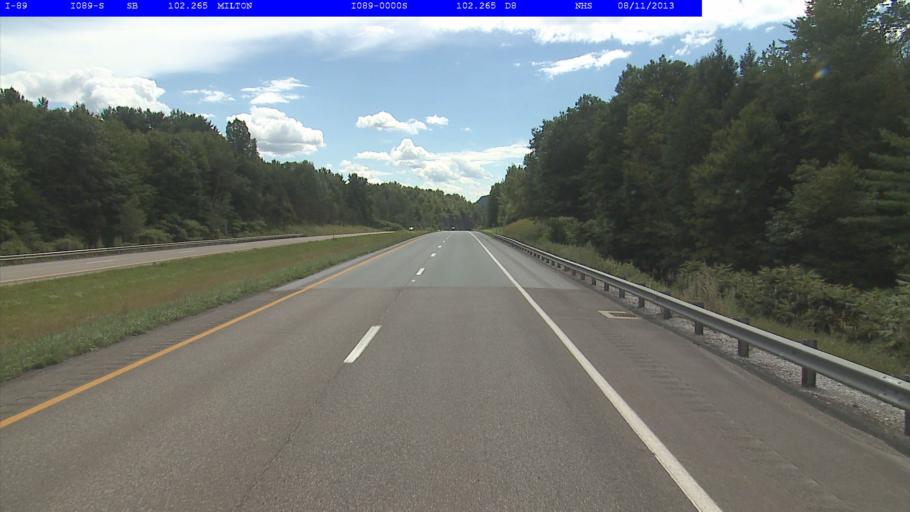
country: US
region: Vermont
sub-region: Chittenden County
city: Milton
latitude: 44.6462
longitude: -73.1402
